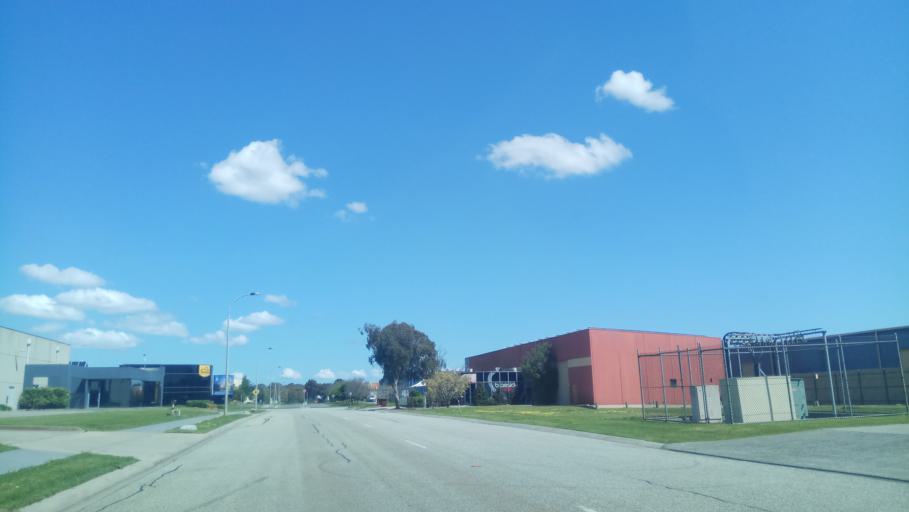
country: AU
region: Victoria
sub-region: Kingston
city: Waterways
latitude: -38.0001
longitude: 145.1163
